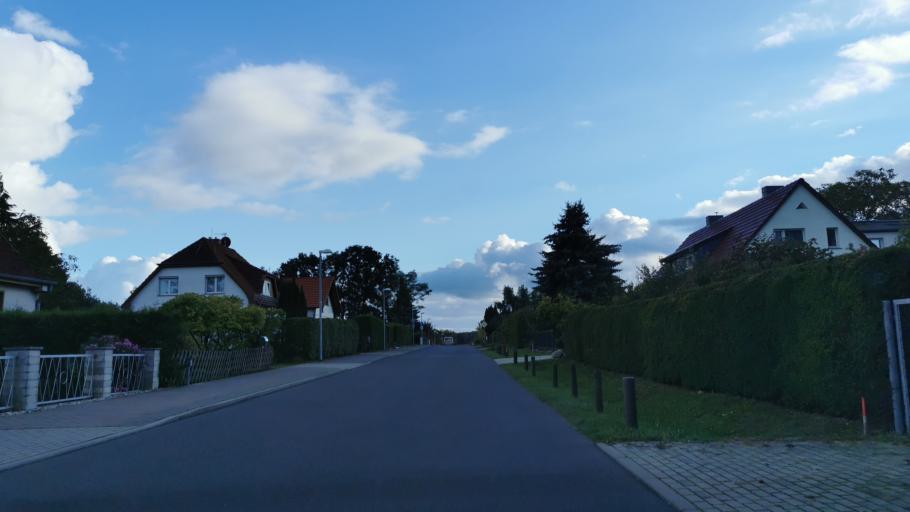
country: DE
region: Brandenburg
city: Werder
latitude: 52.3465
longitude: 12.8832
